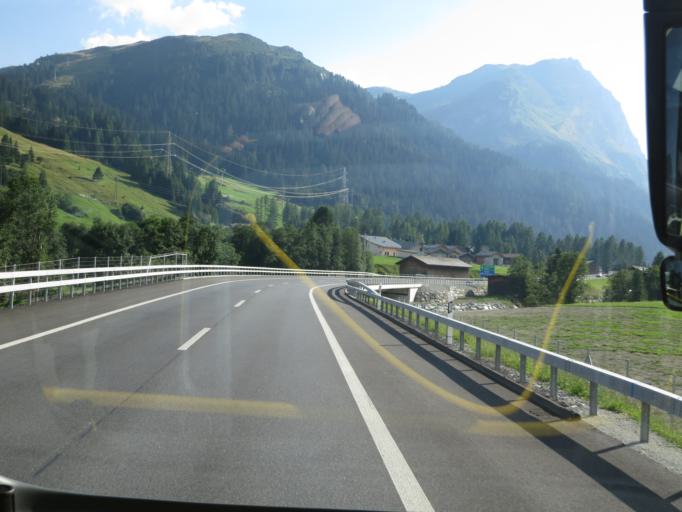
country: CH
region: Grisons
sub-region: Hinterrhein District
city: Hinterrhein
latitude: 46.5537
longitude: 9.3286
